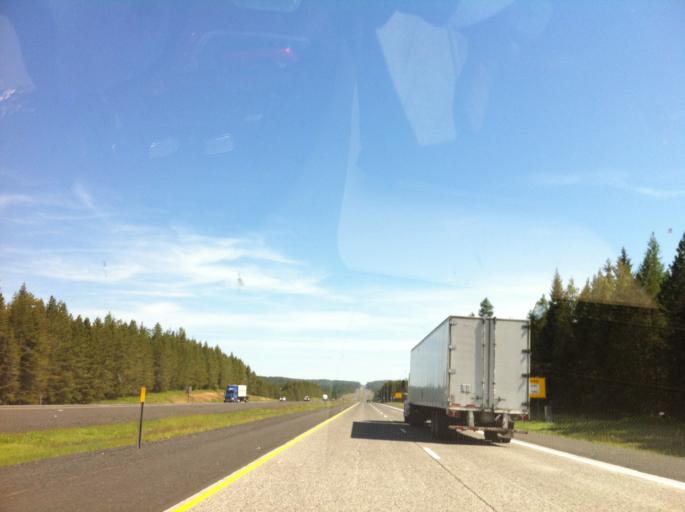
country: US
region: Oregon
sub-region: Umatilla County
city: Mission
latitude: 45.5235
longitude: -118.4419
